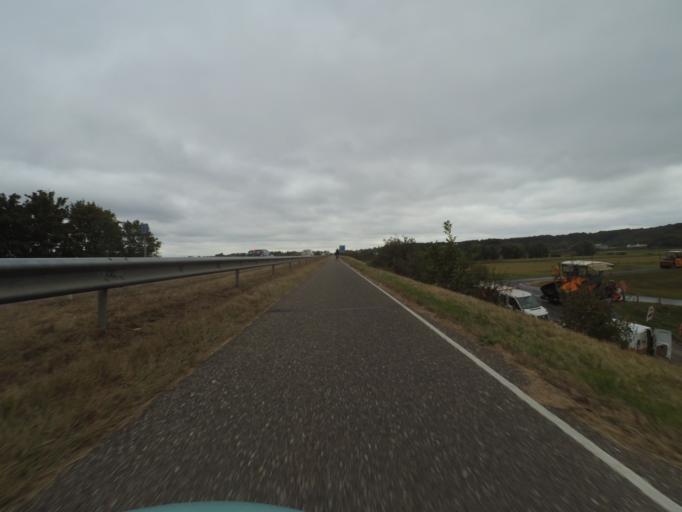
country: NL
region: Utrecht
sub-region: Gemeente Rhenen
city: Rhenen
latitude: 51.9482
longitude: 5.5752
